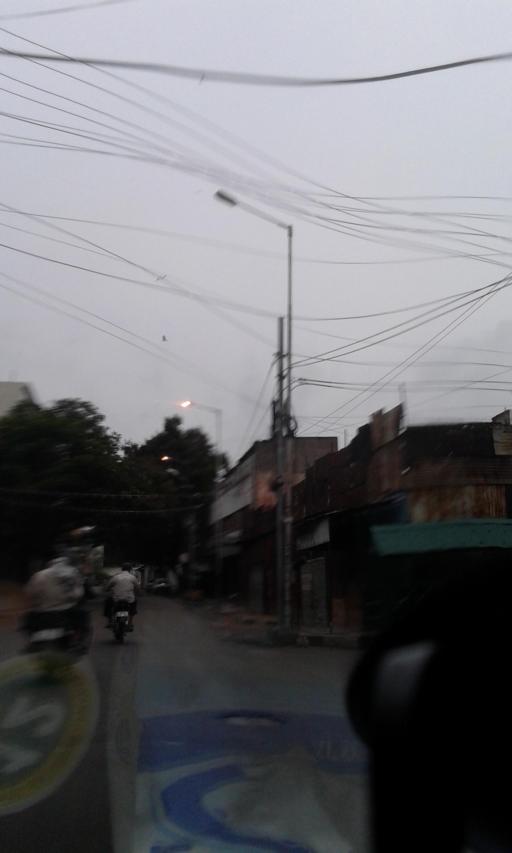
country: IN
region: Telangana
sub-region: Hyderabad
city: Hyderabad
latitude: 17.3683
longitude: 78.4841
